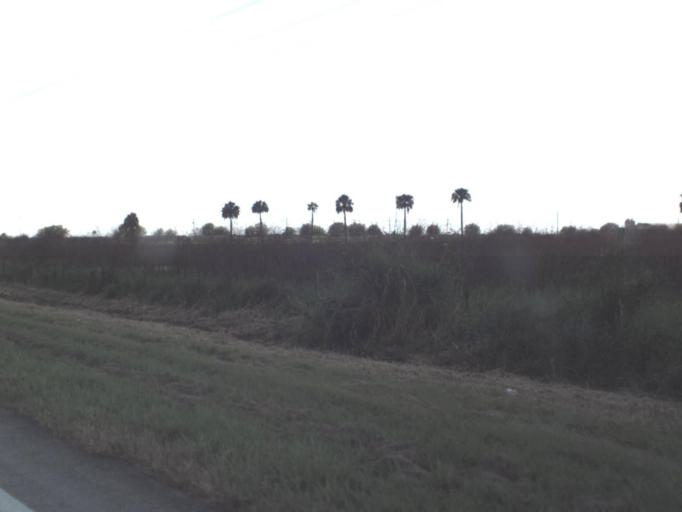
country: US
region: Florida
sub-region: Okeechobee County
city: Okeechobee
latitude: 27.3615
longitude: -80.9662
